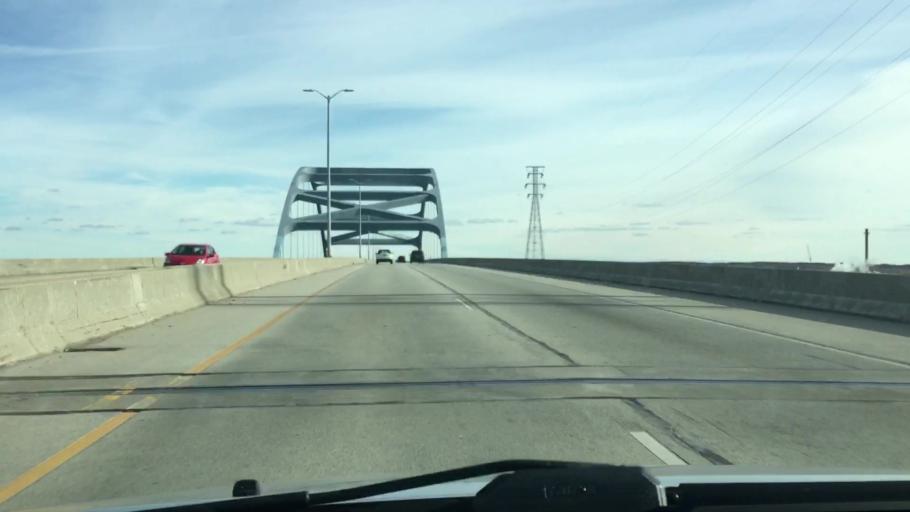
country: US
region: Wisconsin
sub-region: Brown County
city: Green Bay
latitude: 44.5340
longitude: -88.0102
